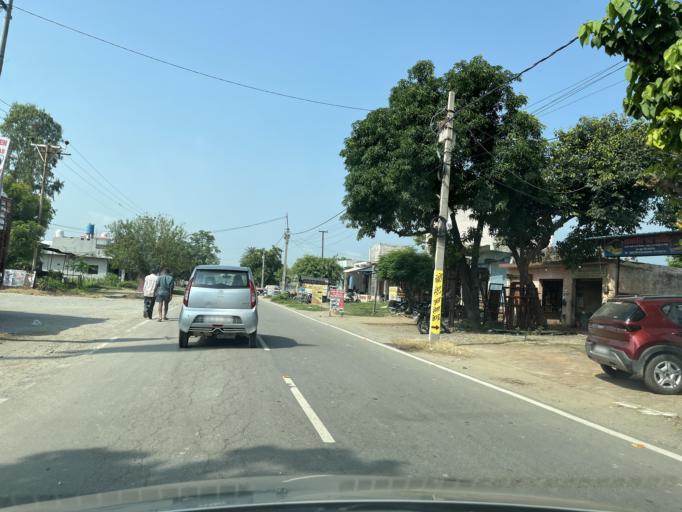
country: IN
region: Uttarakhand
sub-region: Udham Singh Nagar
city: Bazpur
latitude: 29.2078
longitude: 79.2126
